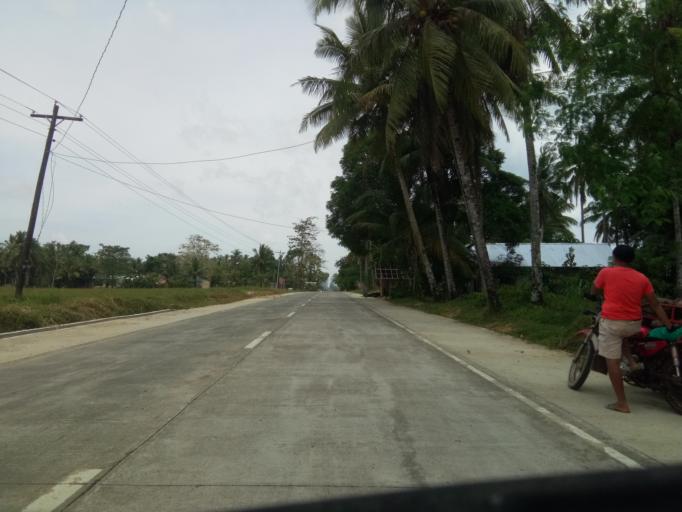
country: PH
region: Caraga
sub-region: Province of Surigao del Norte
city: San Isidro
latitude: 9.9186
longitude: 126.0474
